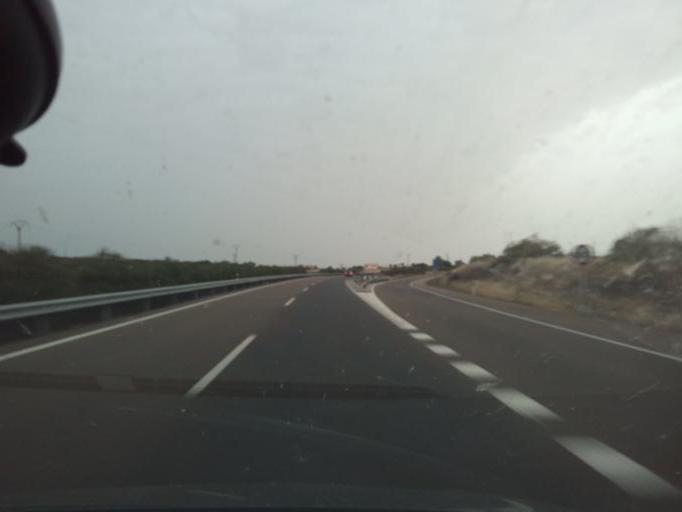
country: ES
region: Extremadura
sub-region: Provincia de Badajoz
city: San Pedro de Merida
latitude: 38.9471
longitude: -6.1761
